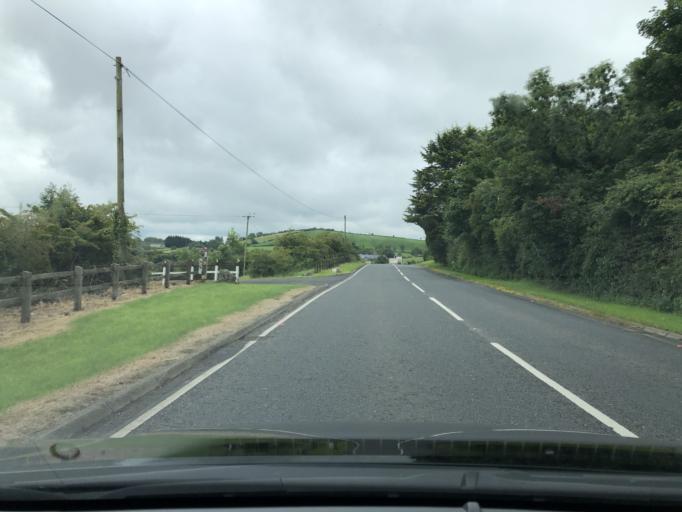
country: GB
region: Northern Ireland
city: Ballynahinch
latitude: 54.3865
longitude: -5.8805
